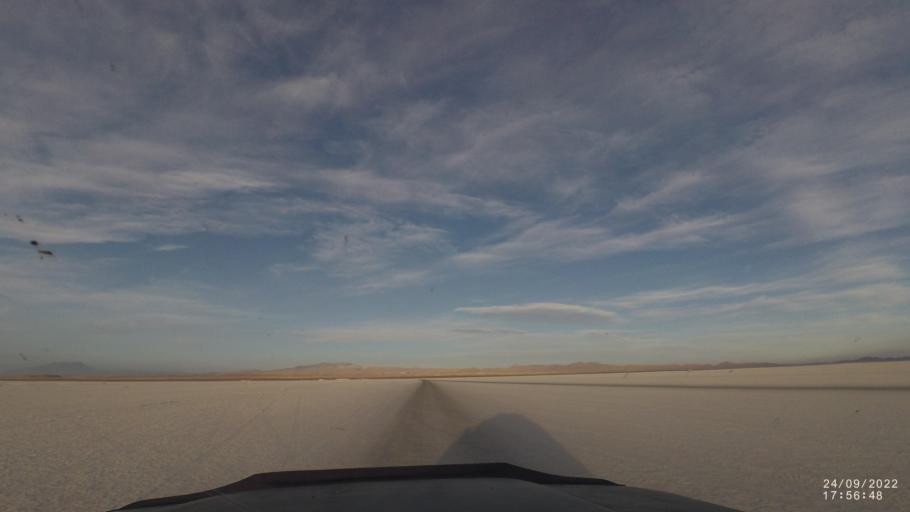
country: BO
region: Potosi
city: Colchani
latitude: -20.3228
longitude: -67.0053
